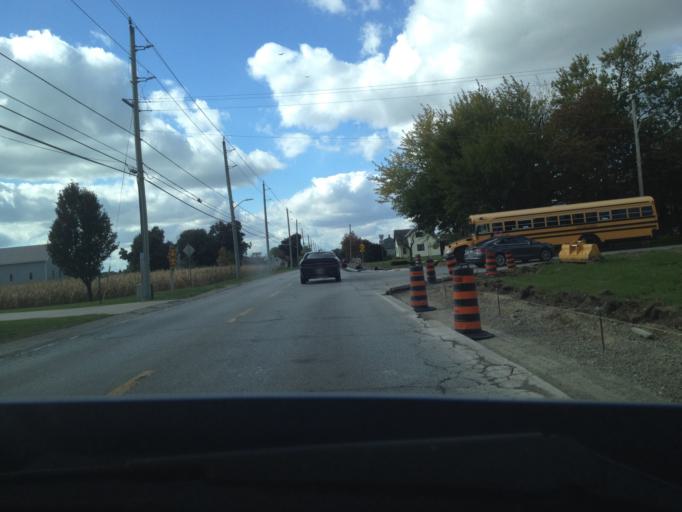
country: CA
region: Ontario
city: Amherstburg
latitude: 42.0348
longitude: -82.6227
